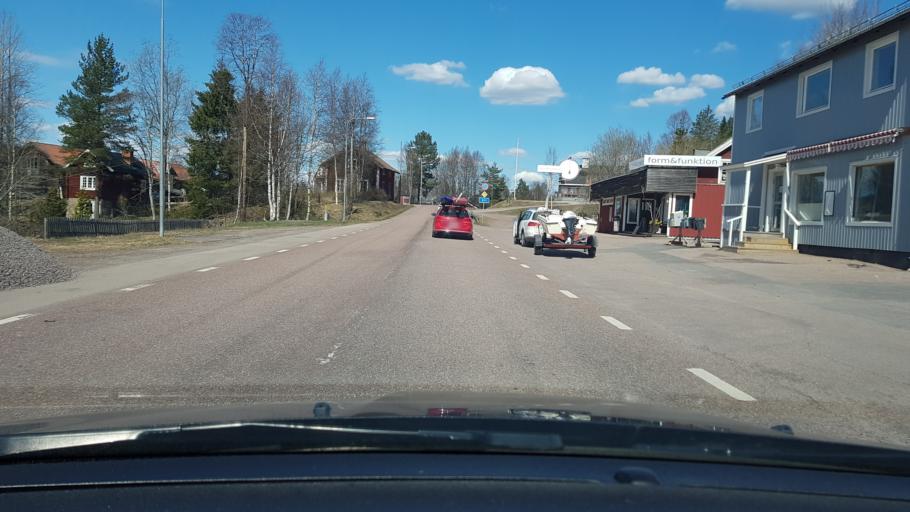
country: SE
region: Dalarna
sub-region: Malung-Saelens kommun
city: Malung
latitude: 61.1616
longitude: 13.2628
